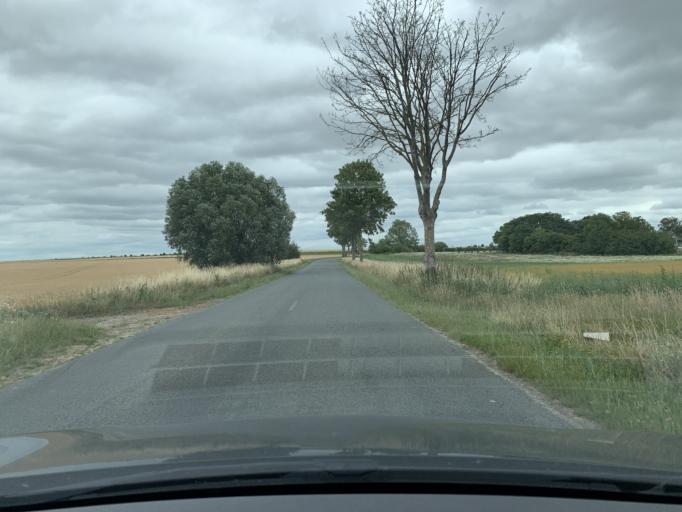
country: FR
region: Nord-Pas-de-Calais
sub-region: Departement du Nord
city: Aubigny-au-Bac
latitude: 50.2322
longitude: 3.1542
